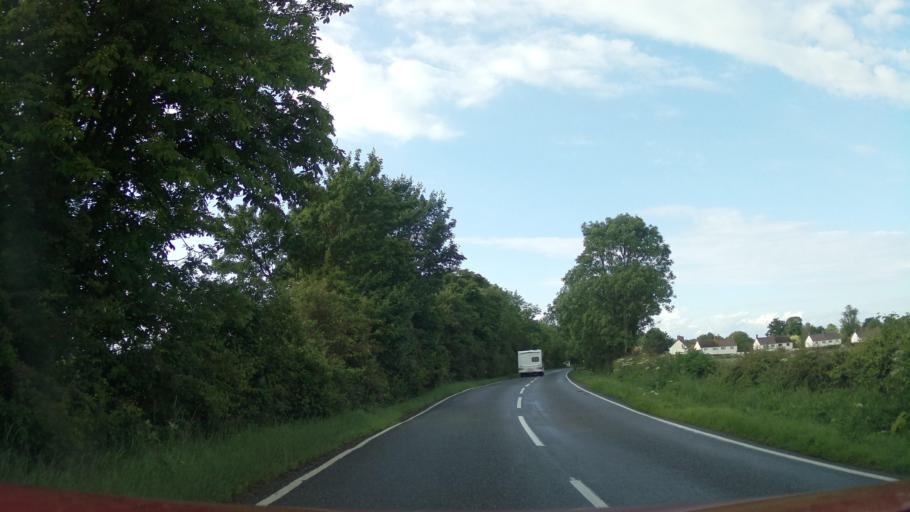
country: GB
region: England
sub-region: Lincolnshire
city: Great Gonerby
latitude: 53.0196
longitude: -0.6581
